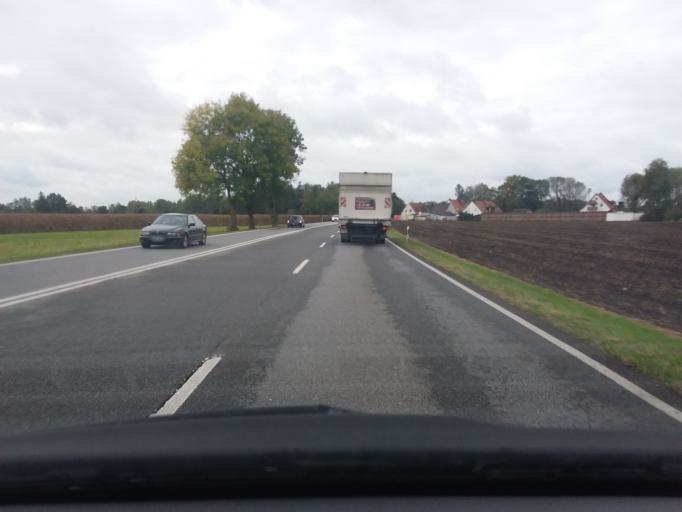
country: DE
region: Bavaria
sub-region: Upper Bavaria
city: Dachau
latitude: 48.2325
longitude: 11.4403
